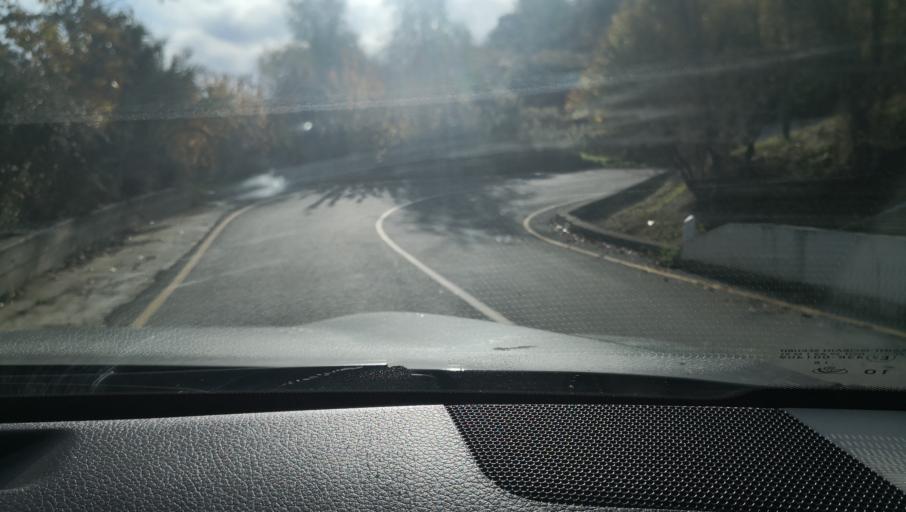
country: CY
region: Lefkosia
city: Lefka
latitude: 35.0229
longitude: 32.7247
